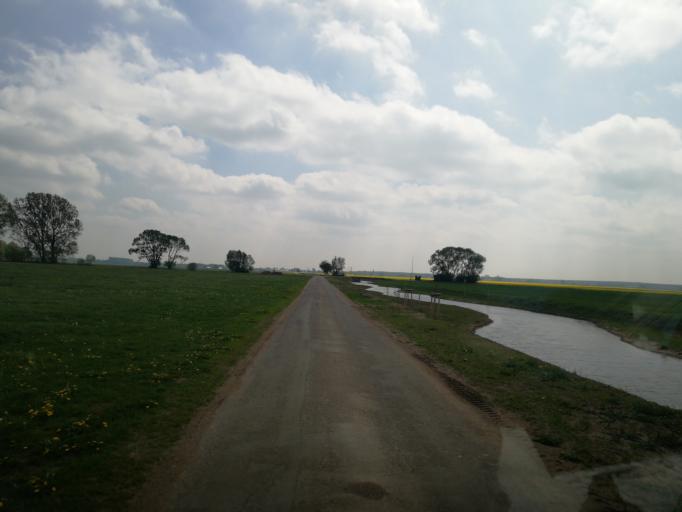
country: DE
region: Brandenburg
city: Doberlug-Kirchhain
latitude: 51.6774
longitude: 13.5363
